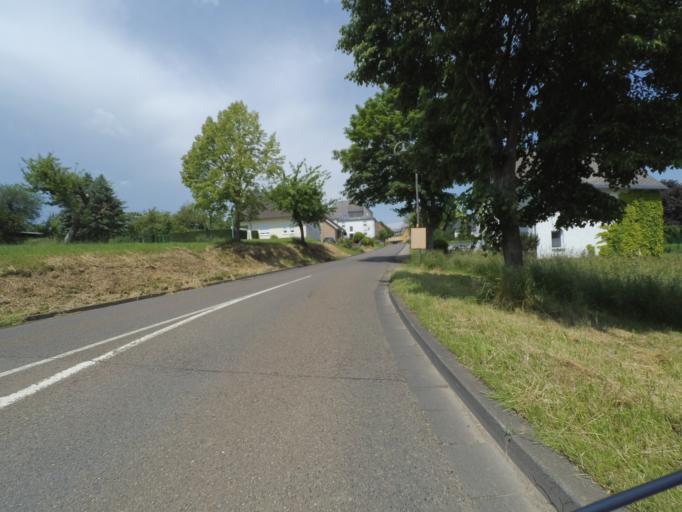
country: DE
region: Rheinland-Pfalz
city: Beulich
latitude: 50.1712
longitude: 7.4536
